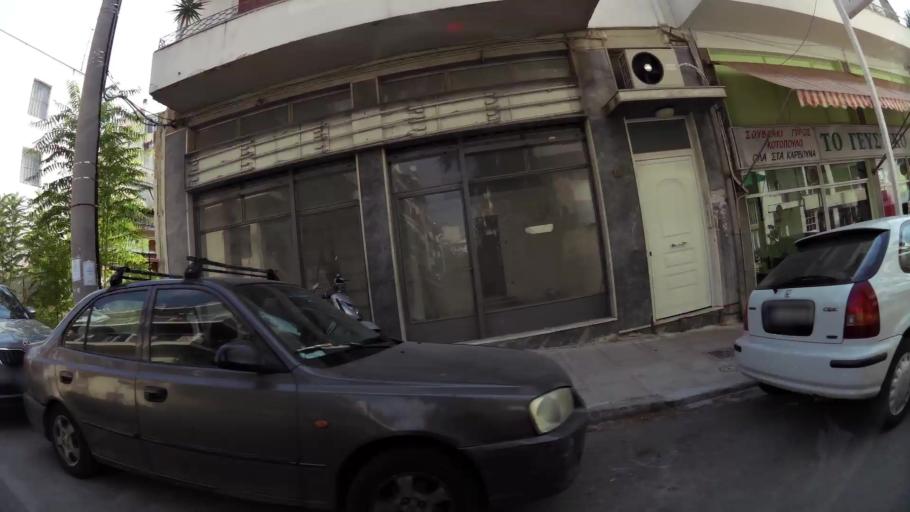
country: GR
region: Attica
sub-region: Nomarchia Athinas
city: Nea Smyrni
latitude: 37.9365
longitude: 23.7131
